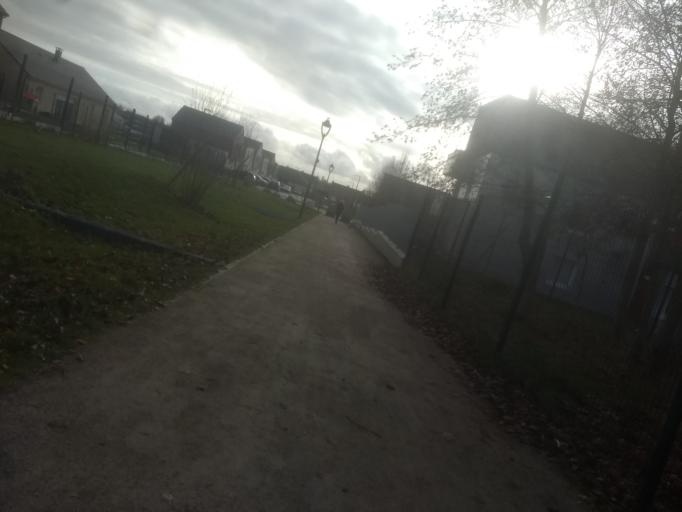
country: FR
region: Nord-Pas-de-Calais
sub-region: Departement du Pas-de-Calais
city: Dainville
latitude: 50.2898
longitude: 2.7331
